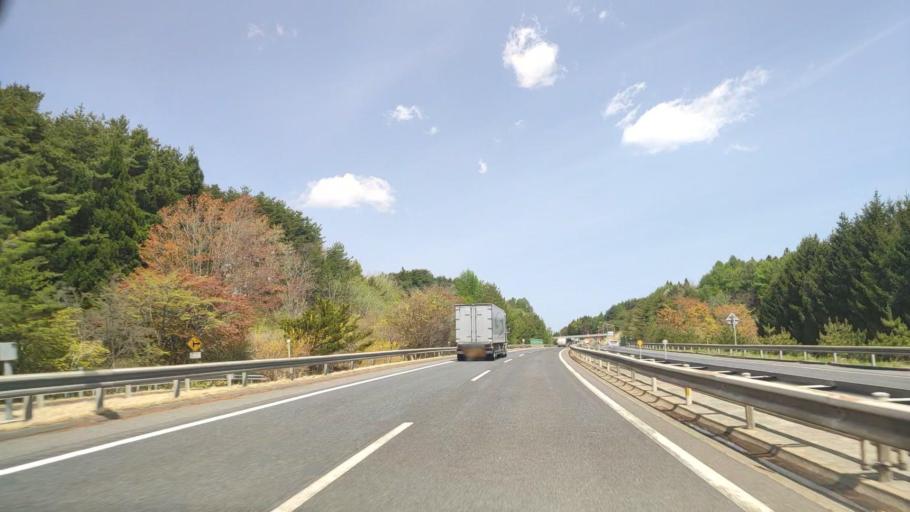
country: JP
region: Aomori
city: Hachinohe
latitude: 40.4055
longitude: 141.4435
